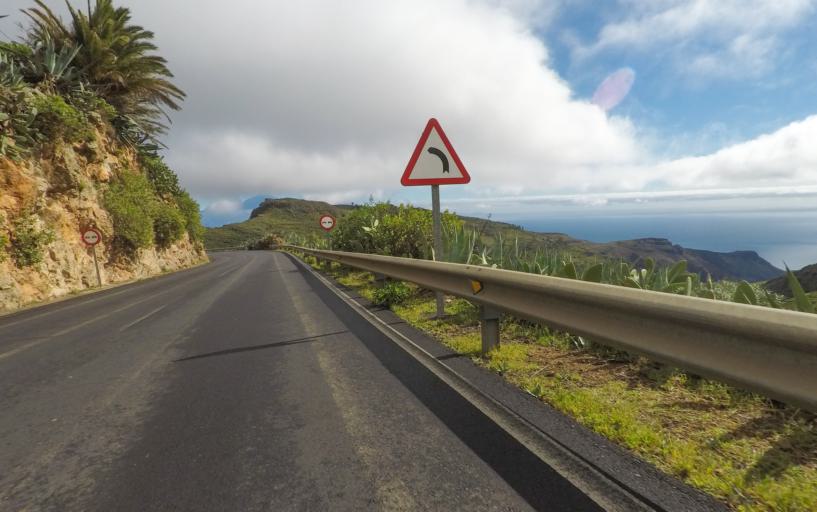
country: ES
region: Canary Islands
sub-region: Provincia de Santa Cruz de Tenerife
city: San Sebastian de la Gomera
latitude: 28.0992
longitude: -17.1726
